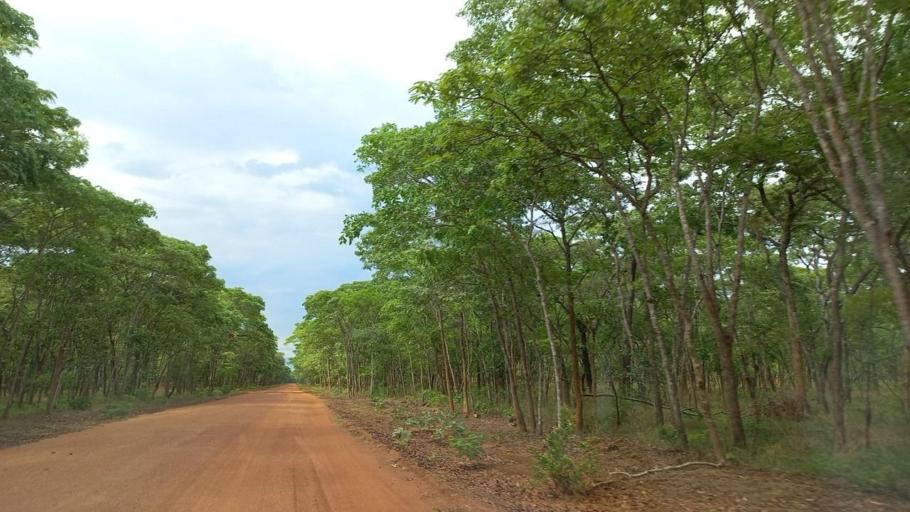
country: ZM
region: North-Western
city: Kalengwa
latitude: -13.4042
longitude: 25.0650
